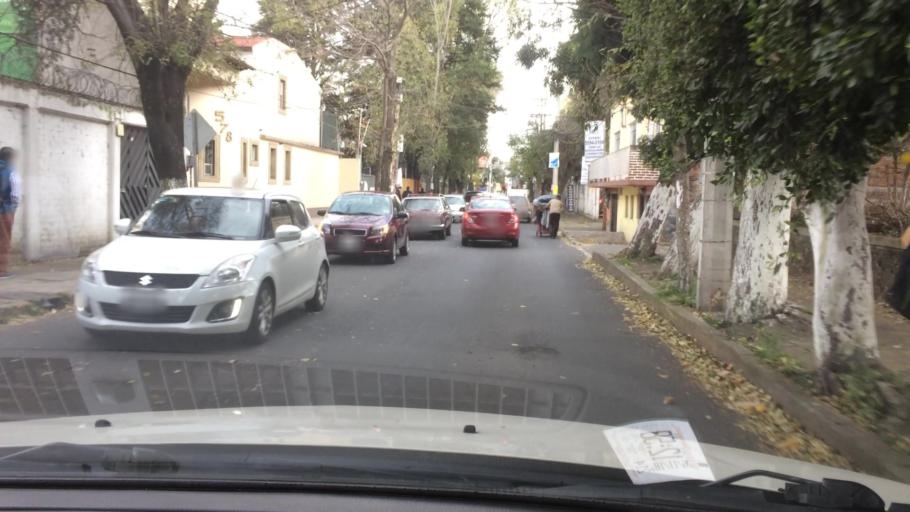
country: MX
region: Mexico City
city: Tlalpan
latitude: 19.2807
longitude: -99.1393
